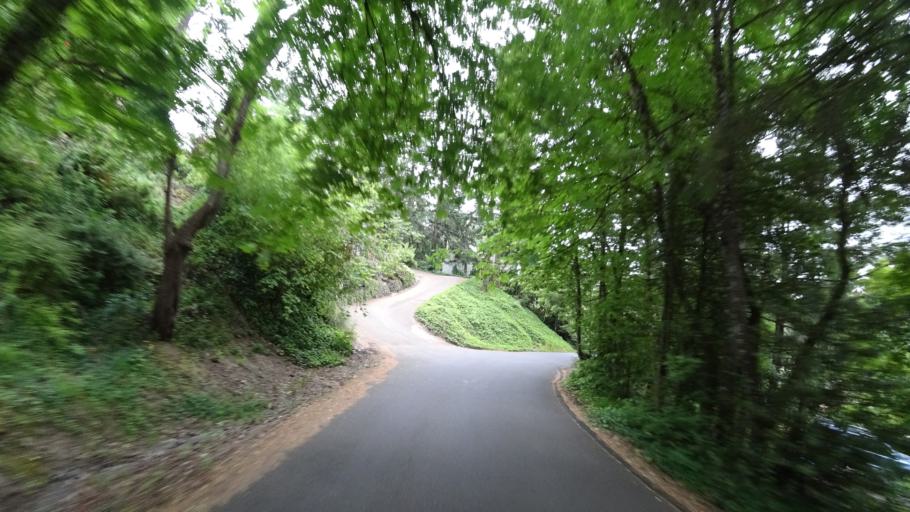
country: US
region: Oregon
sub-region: Multnomah County
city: Portland
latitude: 45.4847
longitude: -122.6957
